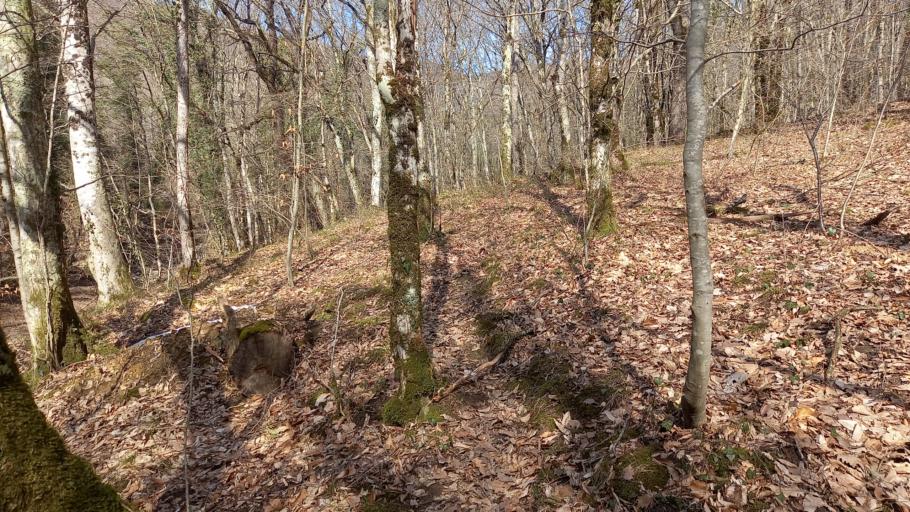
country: RU
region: Krasnodarskiy
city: Arkhipo-Osipovka
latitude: 44.3823
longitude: 38.6016
